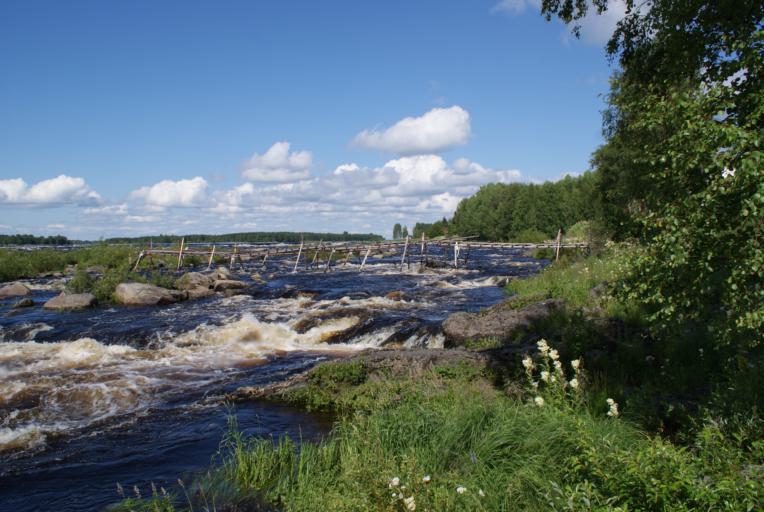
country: FI
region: Lapland
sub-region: Kemi-Tornio
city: Tornio
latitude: 65.9638
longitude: 24.0437
